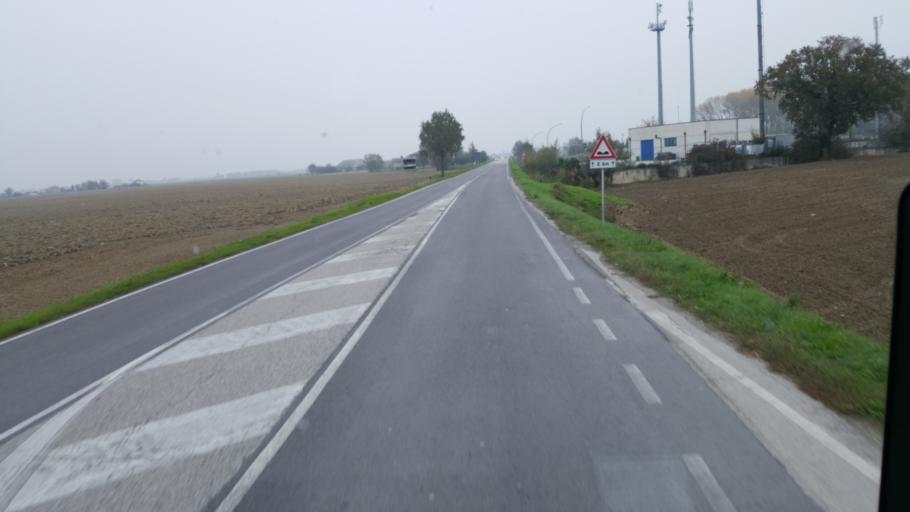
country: IT
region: Veneto
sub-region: Provincia di Rovigo
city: Ficarolo
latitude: 44.9546
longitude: 11.4505
